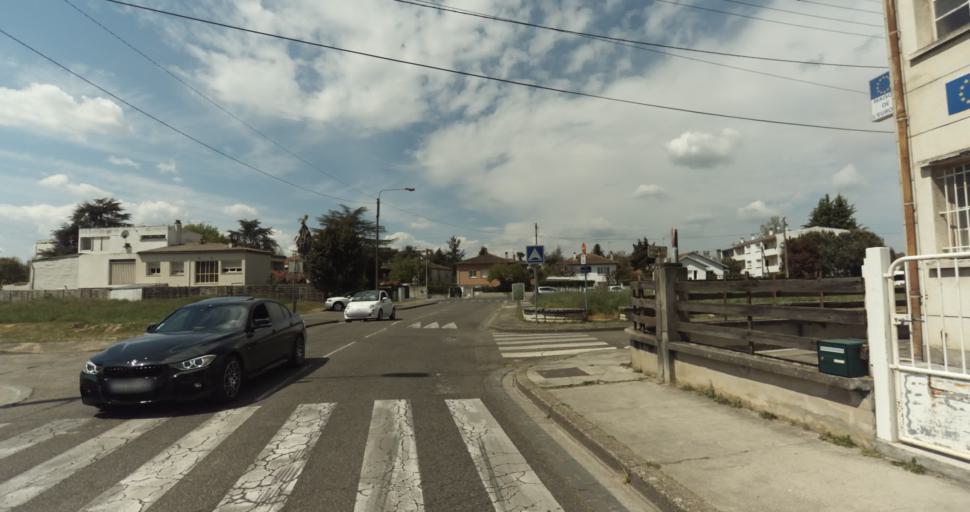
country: FR
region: Aquitaine
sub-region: Departement du Lot-et-Garonne
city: Agen
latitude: 44.1957
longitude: 0.6374
